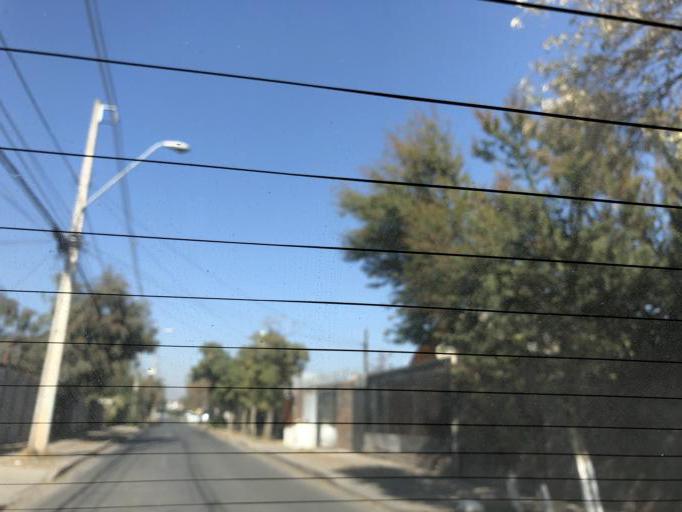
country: CL
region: Santiago Metropolitan
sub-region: Provincia de Cordillera
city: Puente Alto
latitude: -33.6032
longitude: -70.5913
